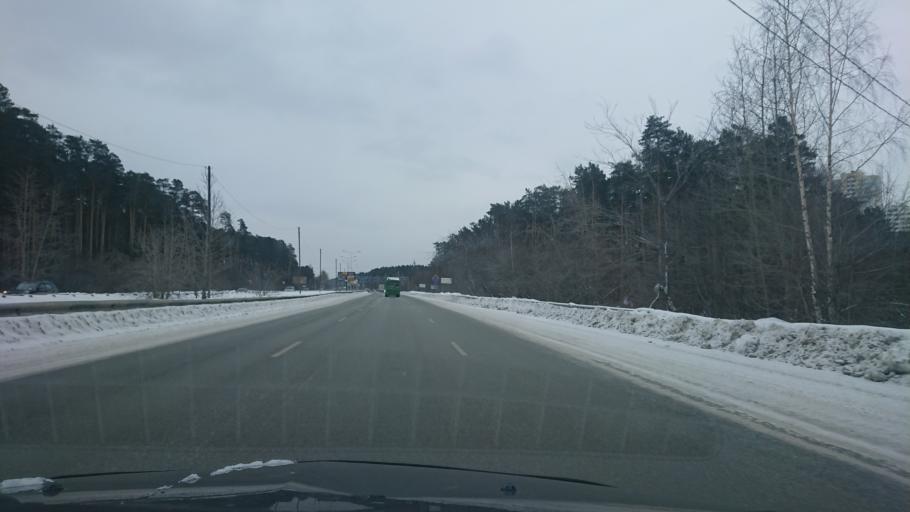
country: RU
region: Sverdlovsk
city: Shirokaya Rechka
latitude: 56.8155
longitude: 60.5125
